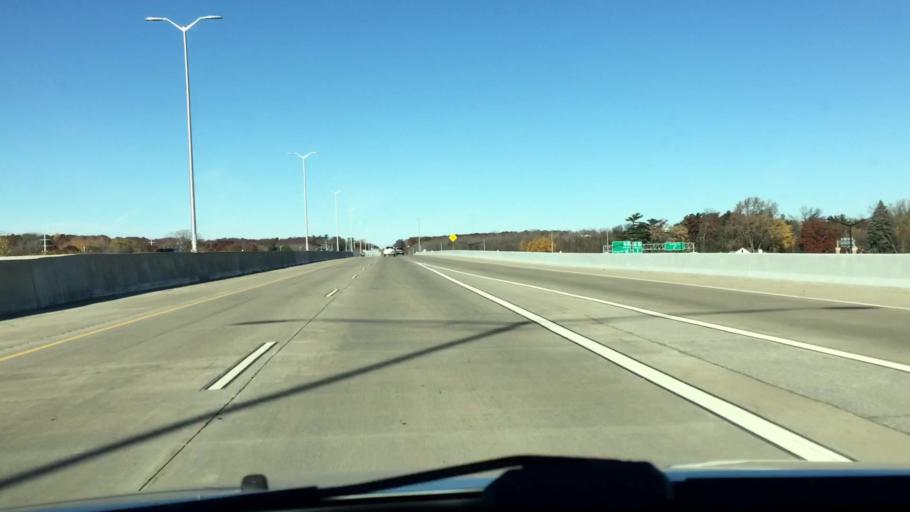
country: US
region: Wisconsin
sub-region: Brown County
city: Howard
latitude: 44.5420
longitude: -88.0853
